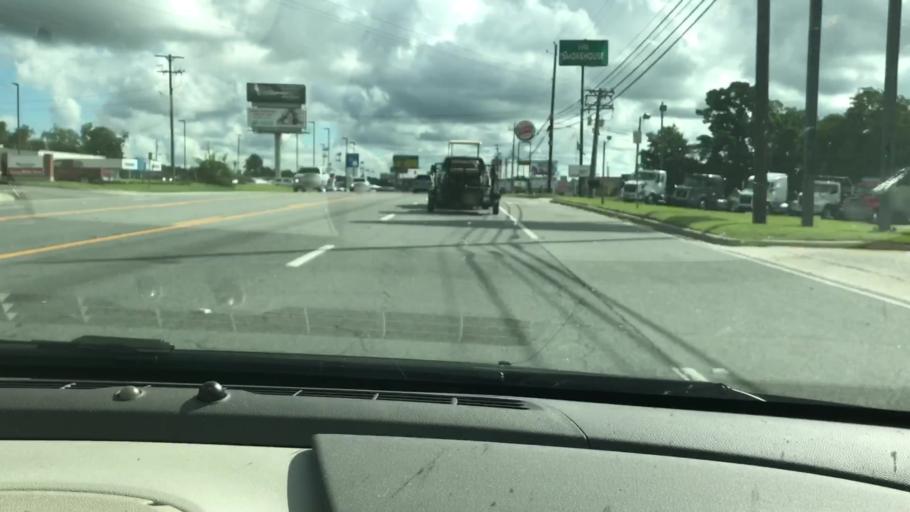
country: US
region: Georgia
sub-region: Tift County
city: Tifton
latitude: 31.4469
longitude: -83.5400
